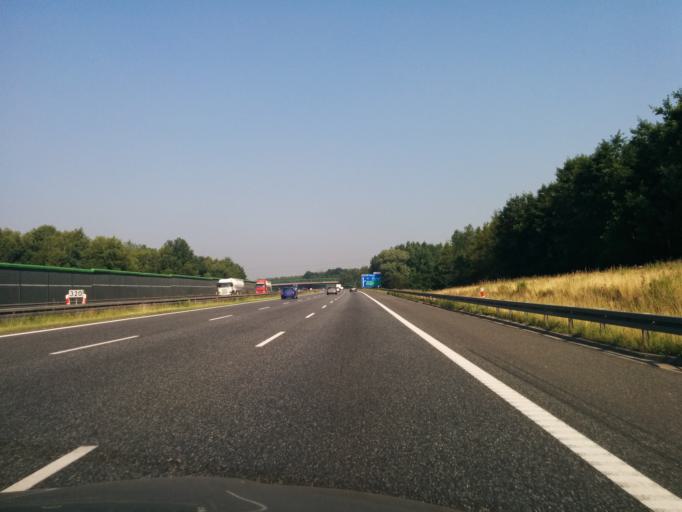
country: PL
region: Silesian Voivodeship
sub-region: Powiat gliwicki
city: Paniowki
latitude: 50.2660
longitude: 18.7785
